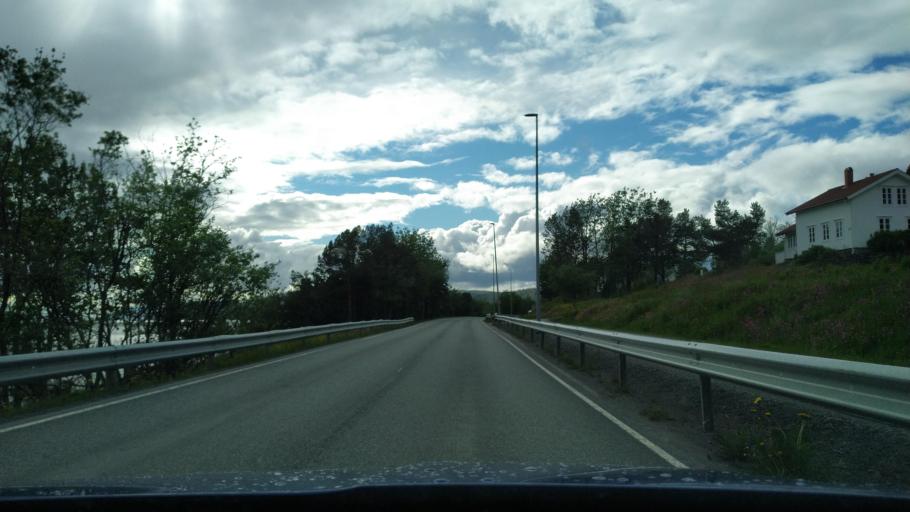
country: NO
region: Troms
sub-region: Sorreisa
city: Sorreisa
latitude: 69.1776
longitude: 18.0771
